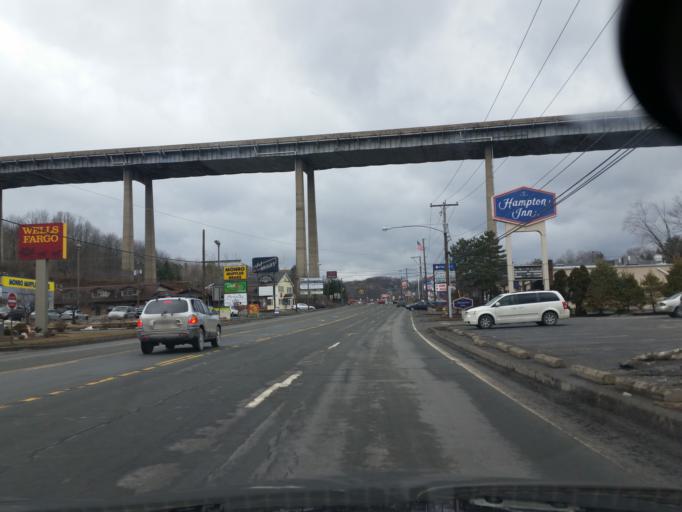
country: US
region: Pennsylvania
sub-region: Lackawanna County
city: Chinchilla
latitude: 41.4822
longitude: -75.6897
